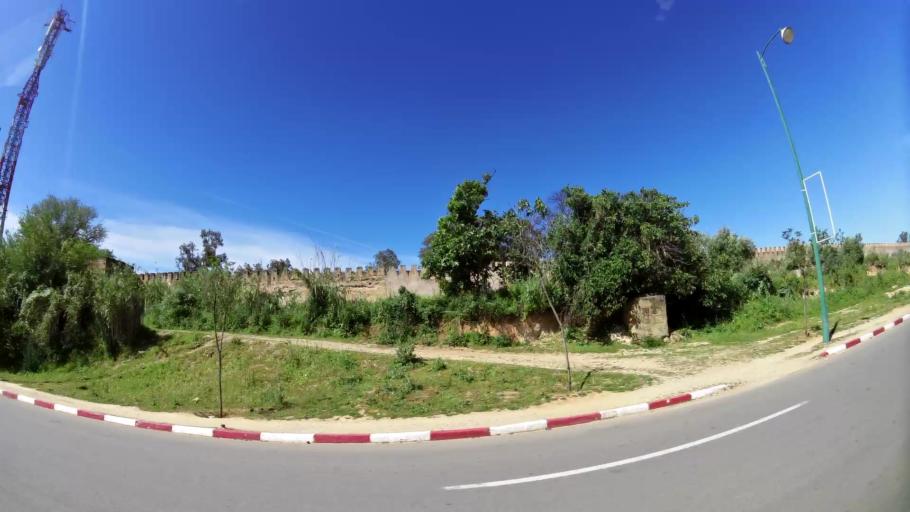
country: MA
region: Meknes-Tafilalet
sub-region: Meknes
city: Meknes
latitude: 33.8773
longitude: -5.5383
